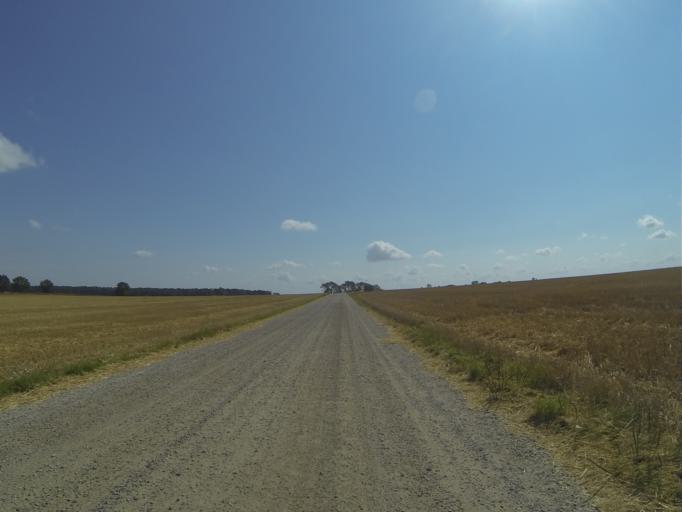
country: SE
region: Skane
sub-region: Lunds Kommun
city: Lund
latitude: 55.7273
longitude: 13.2572
